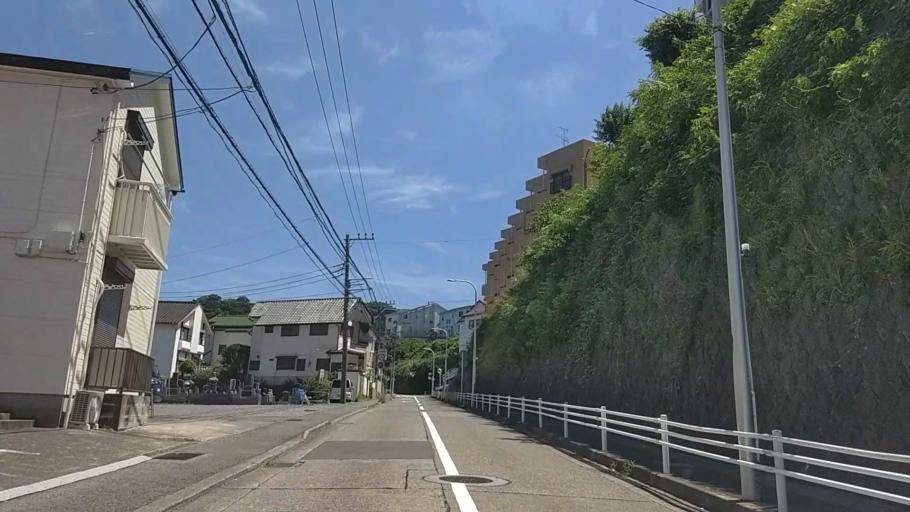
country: JP
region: Kanagawa
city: Zushi
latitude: 35.3060
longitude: 139.5963
